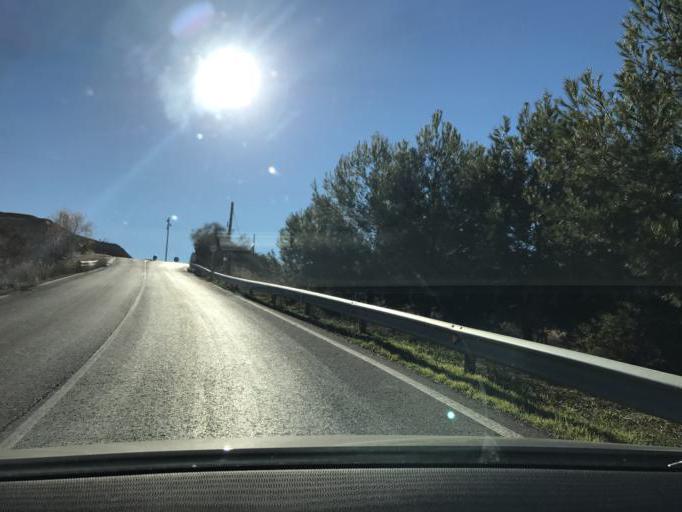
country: ES
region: Andalusia
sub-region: Provincia de Granada
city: Alfacar
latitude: 37.2343
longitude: -3.5694
